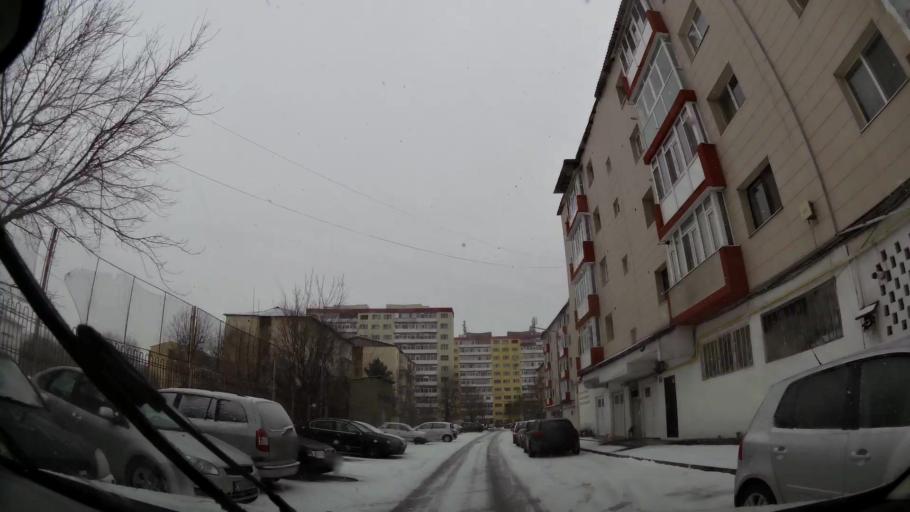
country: RO
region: Dambovita
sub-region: Municipiul Targoviste
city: Targoviste
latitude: 44.9250
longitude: 25.4413
